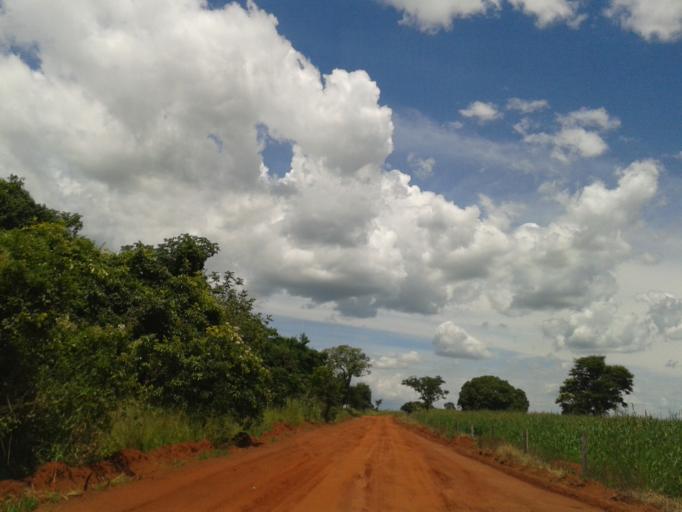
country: BR
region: Minas Gerais
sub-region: Ituiutaba
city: Ituiutaba
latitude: -18.8735
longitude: -49.4833
